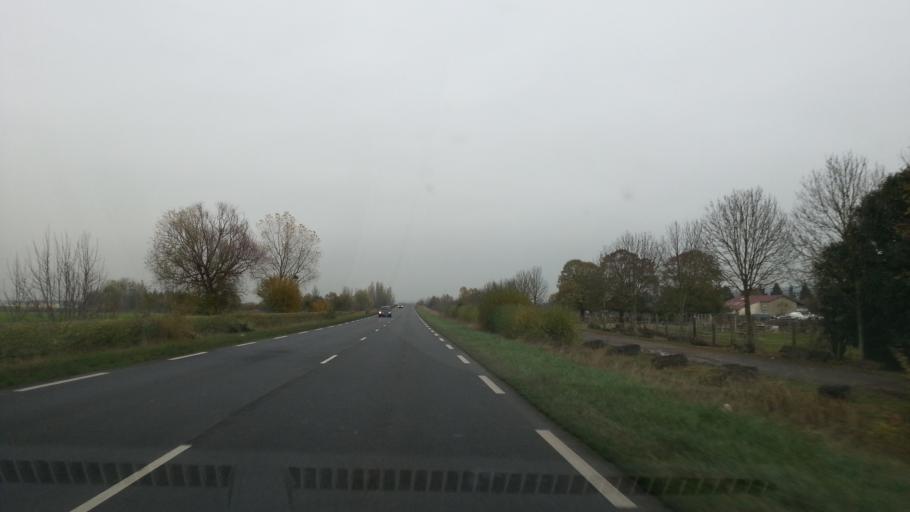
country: FR
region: Ile-de-France
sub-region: Departement du Val-d'Oise
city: Bernes-sur-Oise
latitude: 49.1633
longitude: 2.3024
